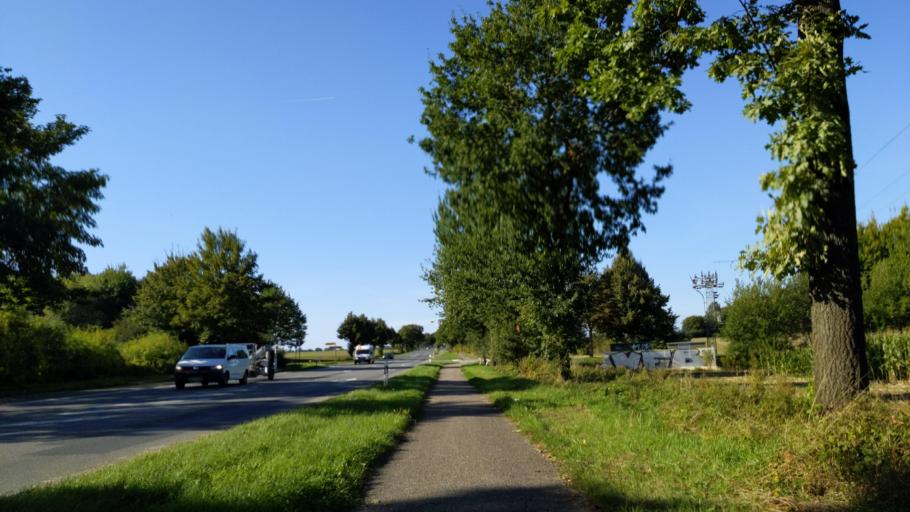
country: DE
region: Schleswig-Holstein
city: Ahrensbok
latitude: 53.9617
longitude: 10.6080
